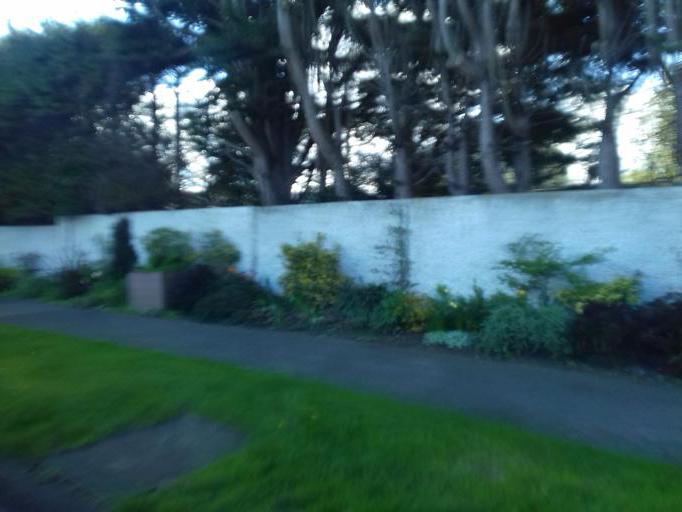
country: IE
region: Leinster
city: Raheny
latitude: 53.3960
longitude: -6.1797
